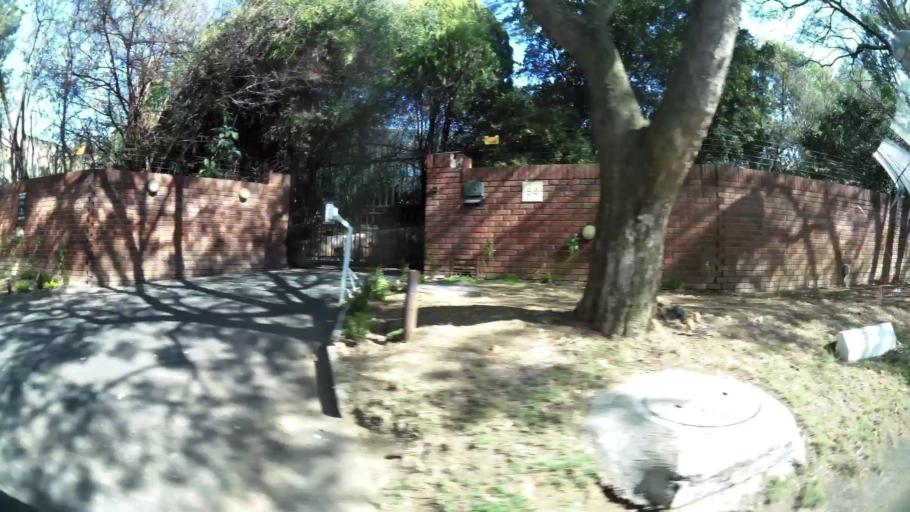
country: ZA
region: Gauteng
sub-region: City of Johannesburg Metropolitan Municipality
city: Johannesburg
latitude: -26.0990
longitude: 28.0295
